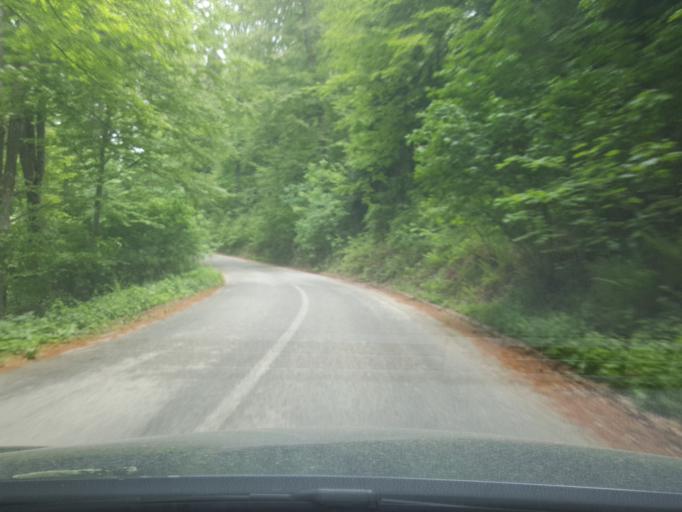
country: RS
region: Central Serbia
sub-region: Zlatiborski Okrug
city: Bajina Basta
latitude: 43.9176
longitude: 19.4913
